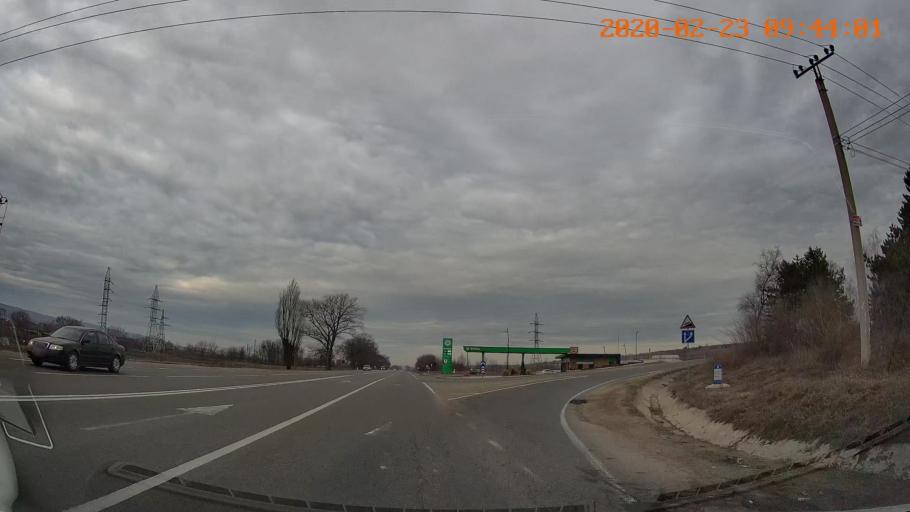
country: MD
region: Orhei
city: Orhei
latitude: 47.3911
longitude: 28.7963
